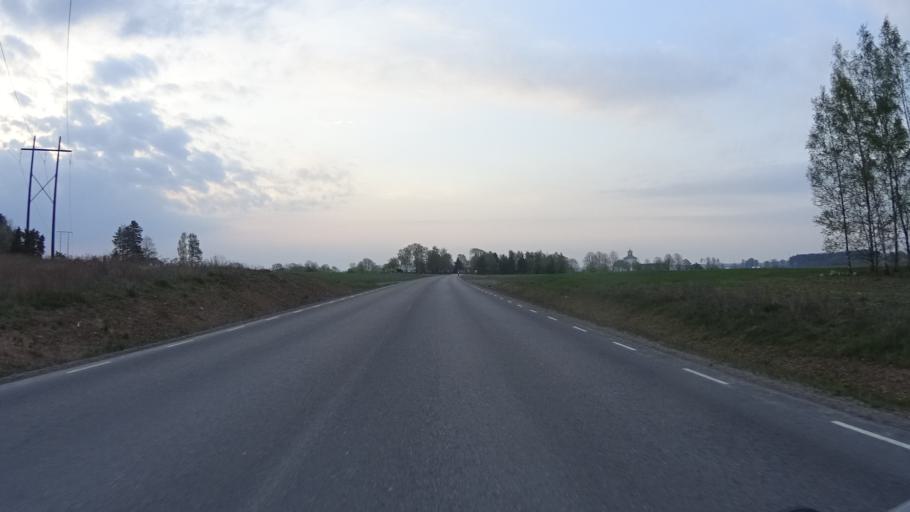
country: SE
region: Vaestra Goetaland
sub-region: Gotene Kommun
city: Kallby
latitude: 58.4972
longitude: 13.3092
